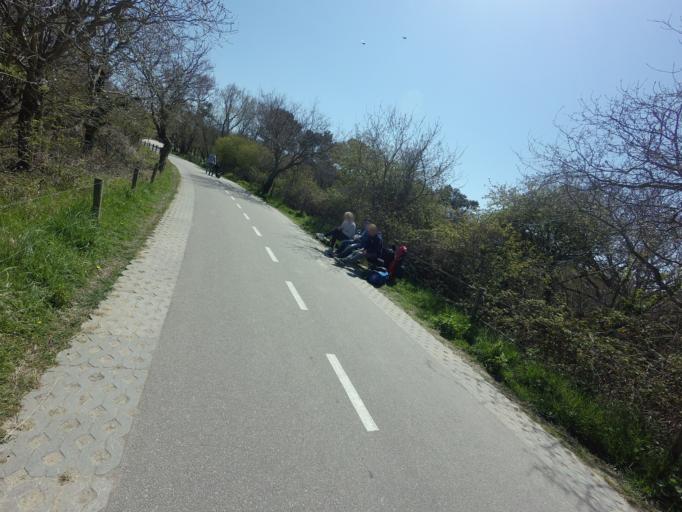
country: NL
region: Zeeland
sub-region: Gemeente Middelburg
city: Middelburg
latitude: 51.5805
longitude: 3.5439
